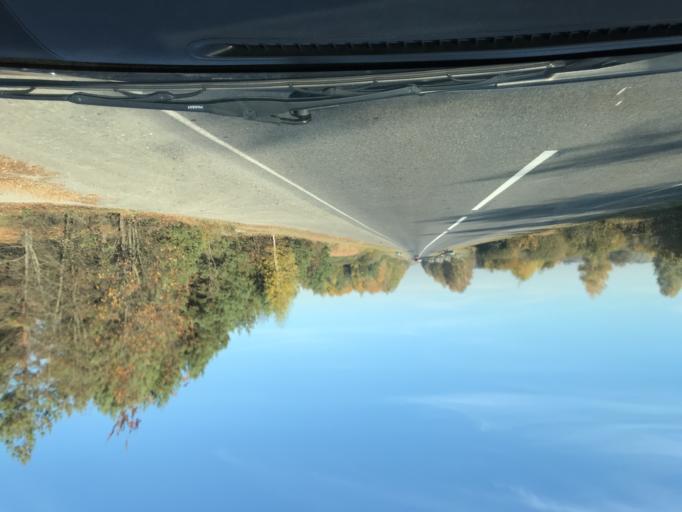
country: BY
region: Brest
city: Luninyets
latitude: 52.2609
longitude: 27.0300
